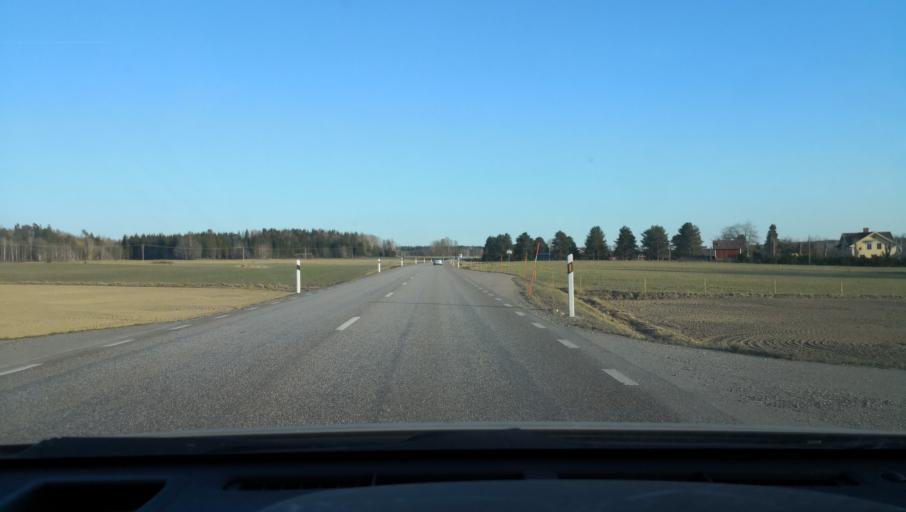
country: SE
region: Uppsala
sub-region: Heby Kommun
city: Heby
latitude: 59.9297
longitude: 16.8744
